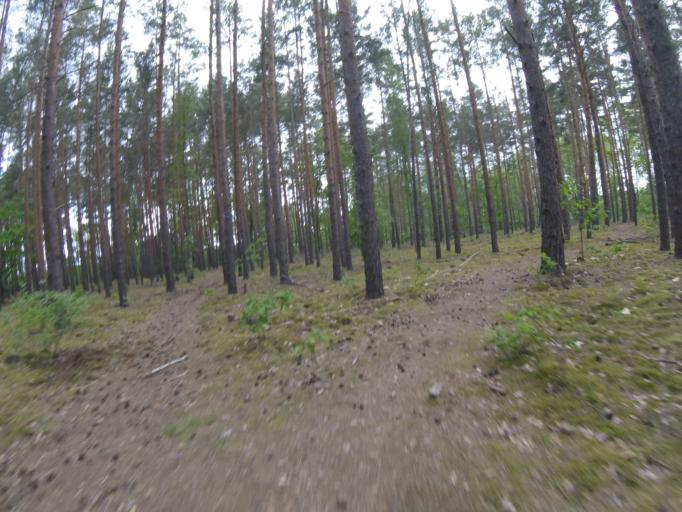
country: DE
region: Brandenburg
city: Bestensee
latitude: 52.2553
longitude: 13.6663
